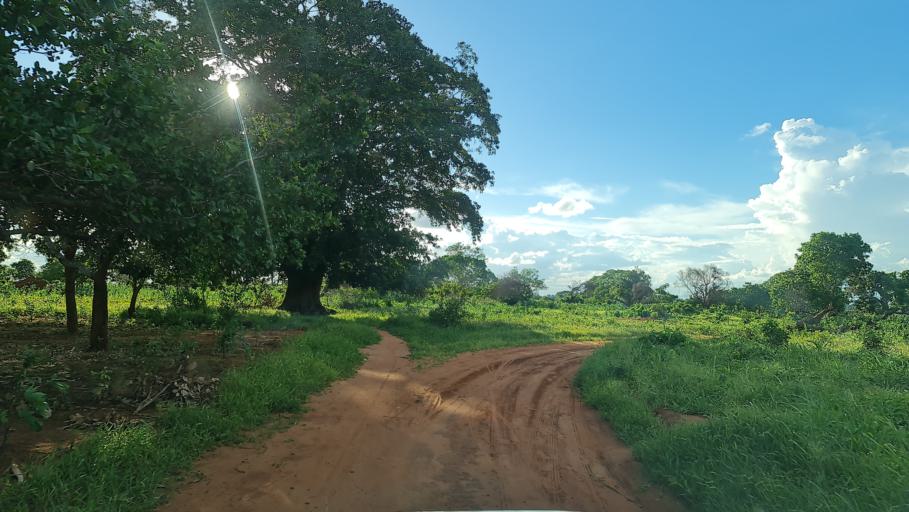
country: MZ
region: Nampula
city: Ilha de Mocambique
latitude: -14.9438
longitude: 40.1574
